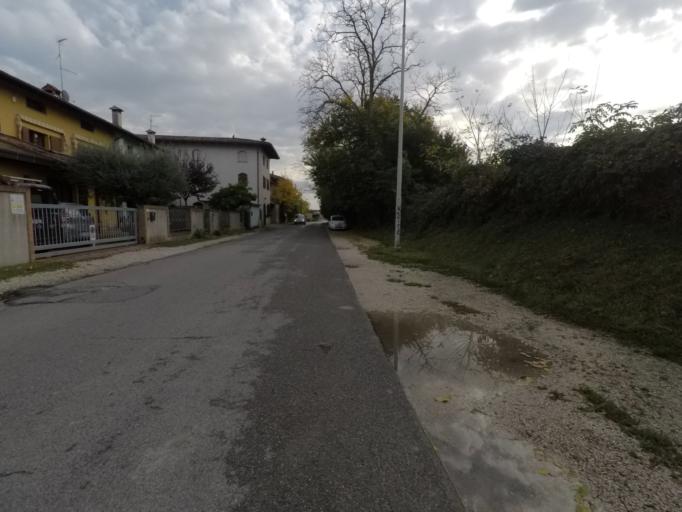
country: IT
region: Friuli Venezia Giulia
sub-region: Provincia di Udine
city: Udine
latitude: 46.0479
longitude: 13.2558
